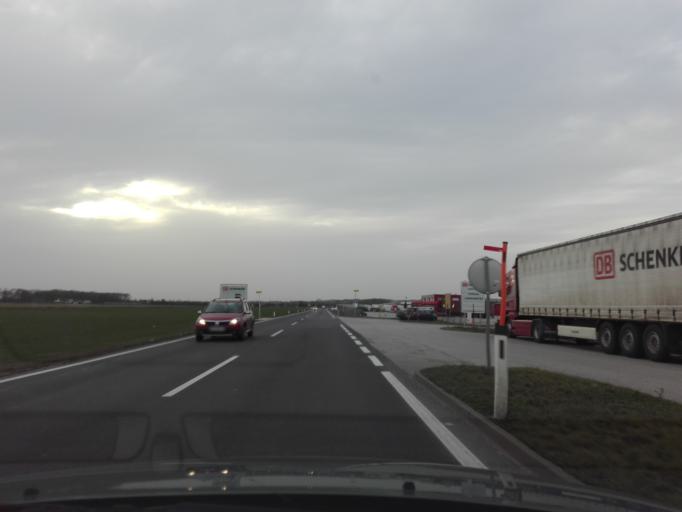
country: AT
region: Upper Austria
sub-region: Politischer Bezirk Linz-Land
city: Horsching
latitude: 48.2351
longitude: 14.1747
